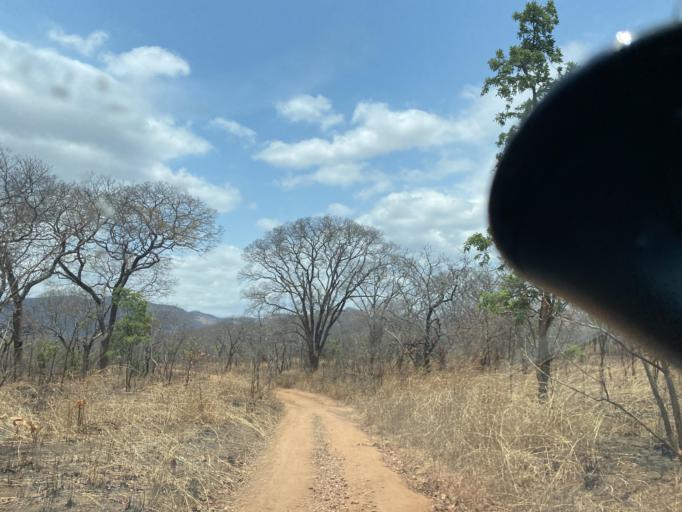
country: ZM
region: Lusaka
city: Luangwa
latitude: -15.1759
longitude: 29.7130
